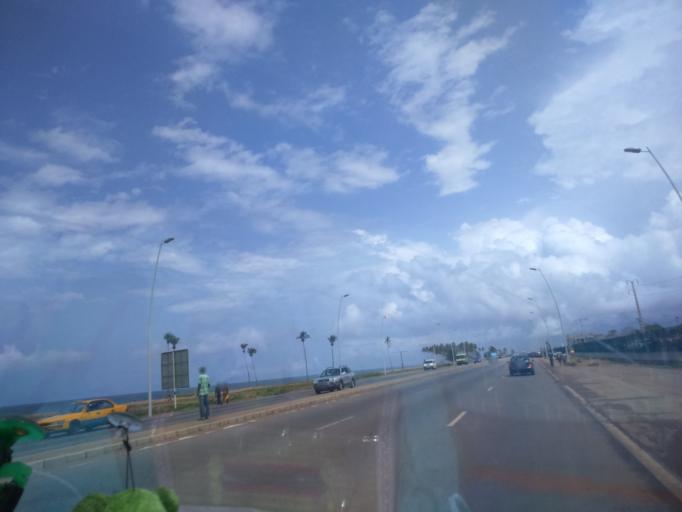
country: CI
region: Lagunes
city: Bingerville
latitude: 5.2382
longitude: -3.8882
